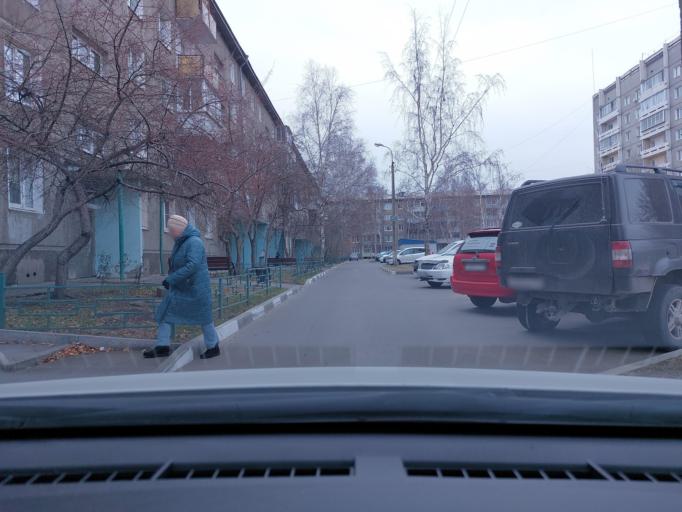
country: RU
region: Irkutsk
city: Smolenshchina
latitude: 52.3460
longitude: 104.1646
